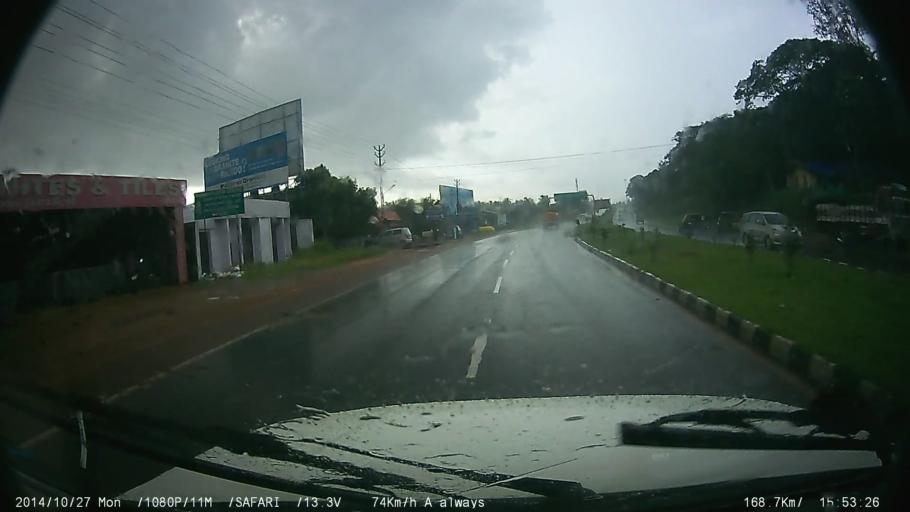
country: IN
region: Kerala
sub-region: Thrissur District
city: Kizhake Chalakudi
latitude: 10.2636
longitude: 76.3536
